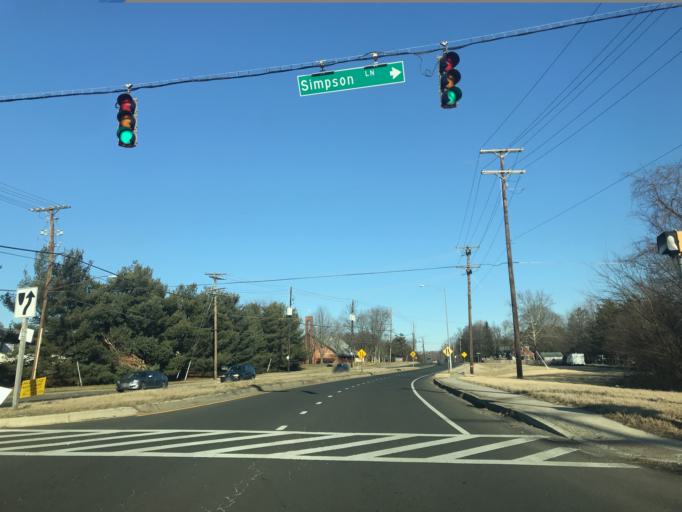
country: US
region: Maryland
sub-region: Prince George's County
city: Clinton
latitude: 38.7695
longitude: -76.8820
